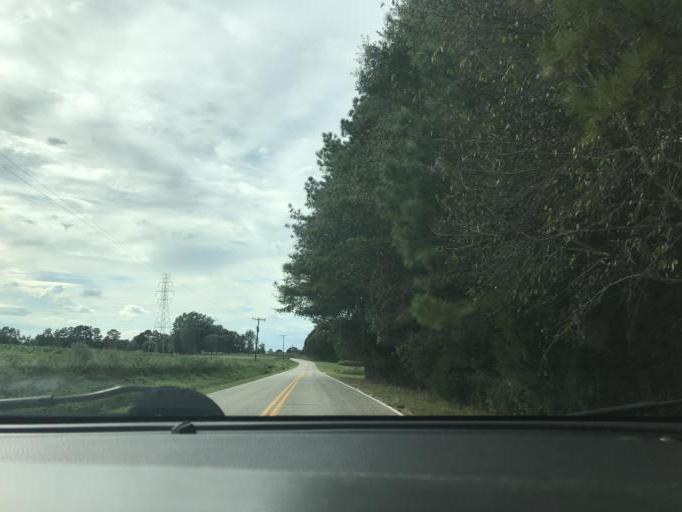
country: US
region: North Carolina
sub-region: Cleveland County
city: Boiling Springs
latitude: 35.1776
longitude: -81.7175
